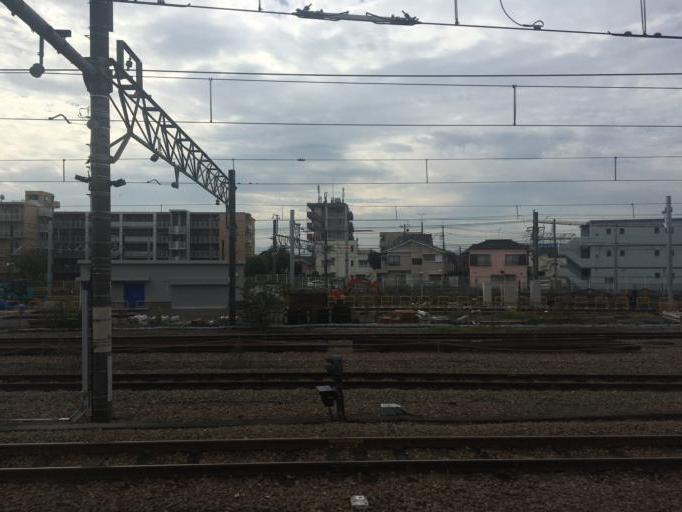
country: JP
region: Tokyo
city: Fussa
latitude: 35.7194
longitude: 139.3455
